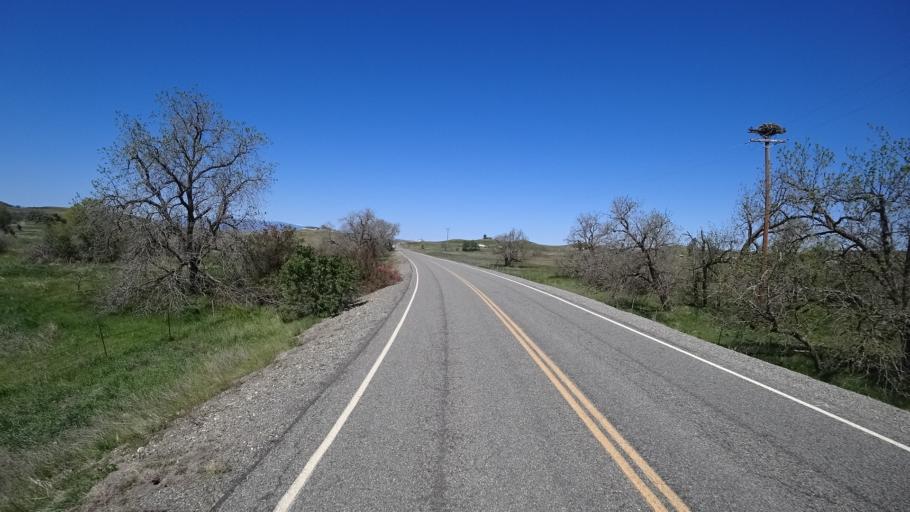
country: US
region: California
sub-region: Glenn County
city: Orland
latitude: 39.8198
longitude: -122.3265
